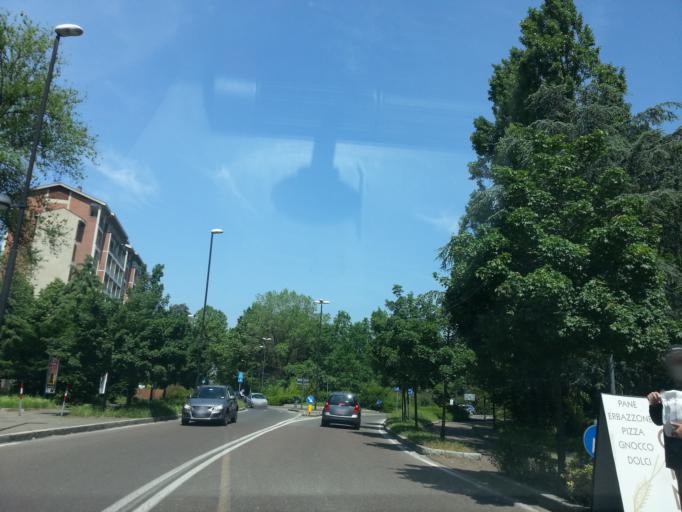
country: IT
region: Emilia-Romagna
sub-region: Provincia di Reggio Emilia
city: Reggio nell'Emilia
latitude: 44.6851
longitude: 10.6359
